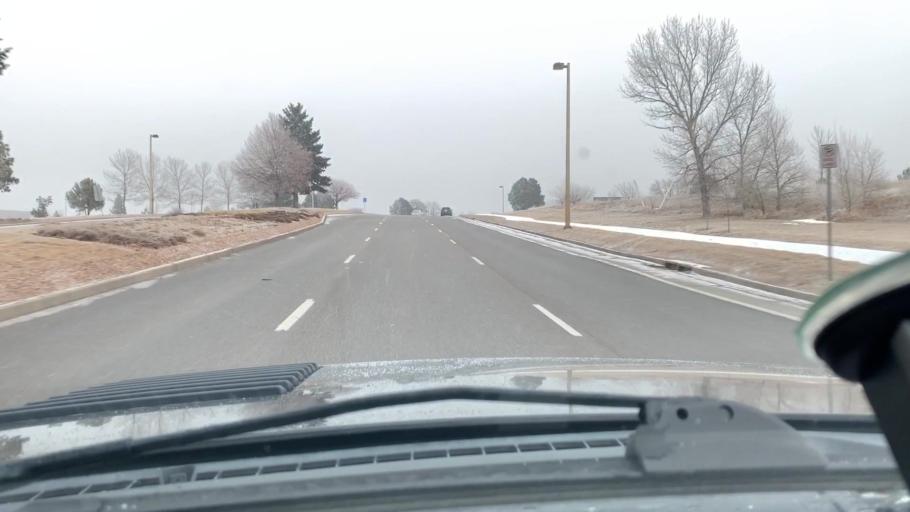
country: US
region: Colorado
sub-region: Arapahoe County
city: Dove Valley
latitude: 39.5786
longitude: -104.8381
